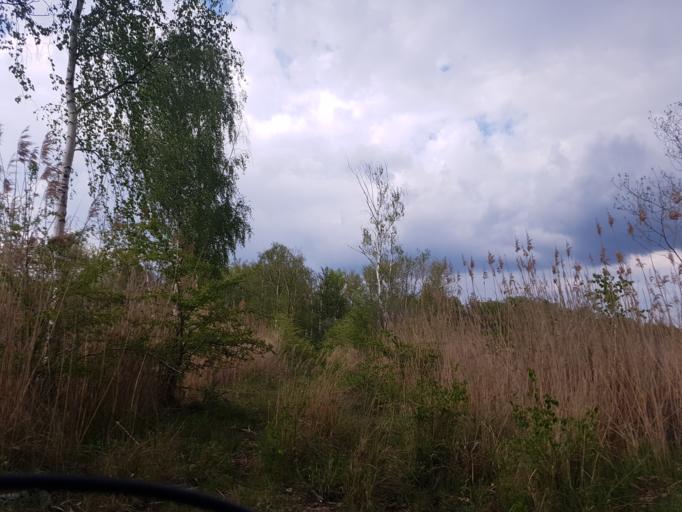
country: DE
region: Brandenburg
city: Schilda
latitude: 51.5932
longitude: 13.4071
